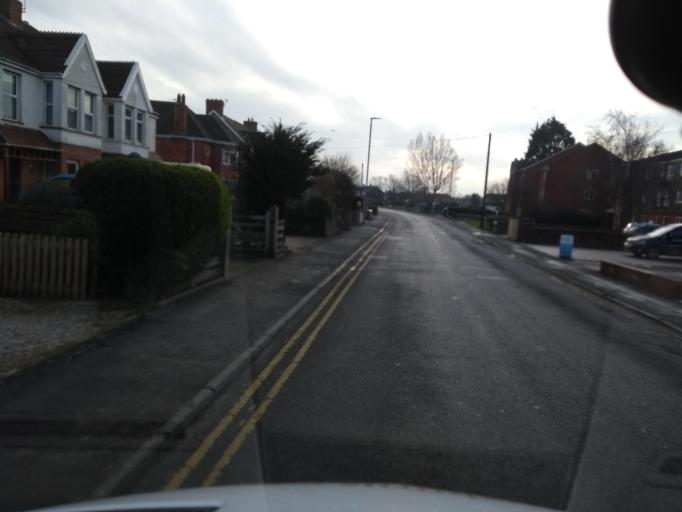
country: GB
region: England
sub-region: Somerset
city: Burnham-on-Sea
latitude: 51.2322
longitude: -2.9926
